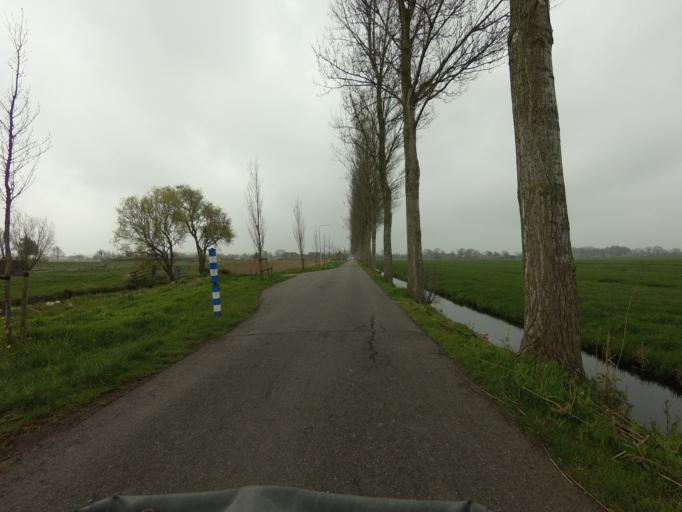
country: NL
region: South Holland
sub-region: Gemeente Vlist
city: Haastrecht
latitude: 52.0200
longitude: 4.8056
